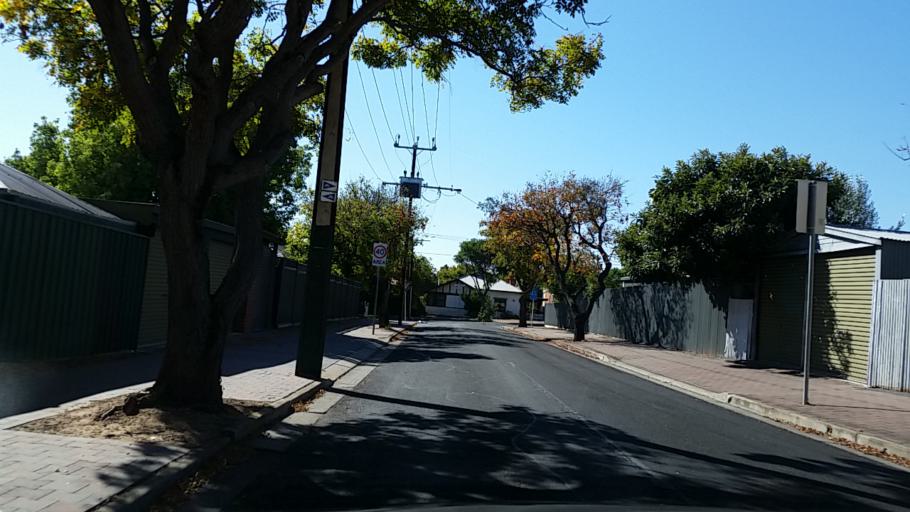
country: AU
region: South Australia
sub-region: Prospect
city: Prospect
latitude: -34.8821
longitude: 138.5892
